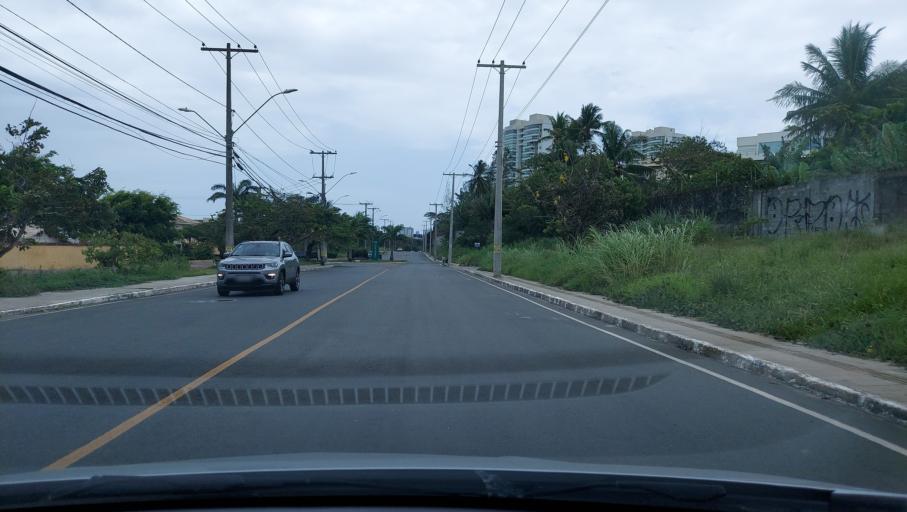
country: BR
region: Bahia
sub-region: Lauro De Freitas
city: Lauro de Freitas
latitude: -12.9489
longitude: -38.3857
